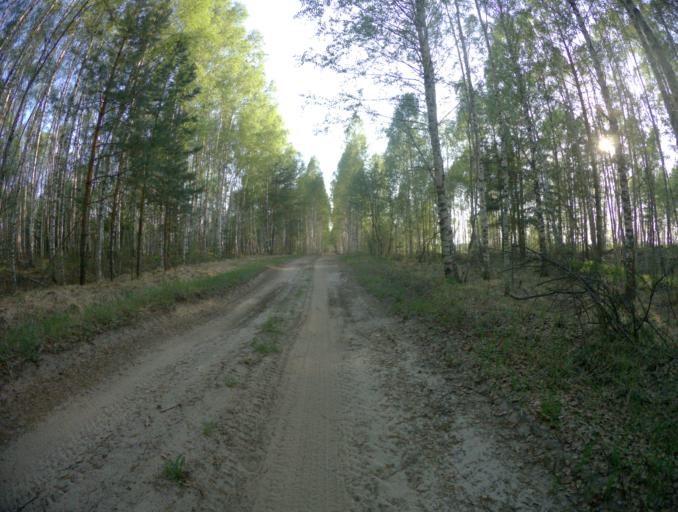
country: RU
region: Vladimir
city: Vyazniki
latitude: 56.3722
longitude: 42.1652
